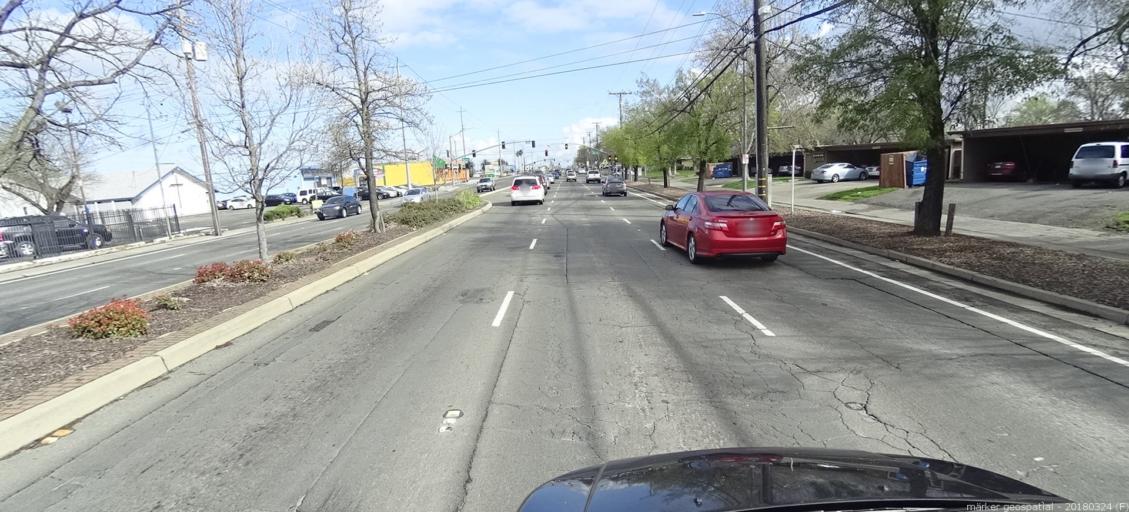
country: US
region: California
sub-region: Sacramento County
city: North Highlands
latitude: 38.6727
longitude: -121.3828
